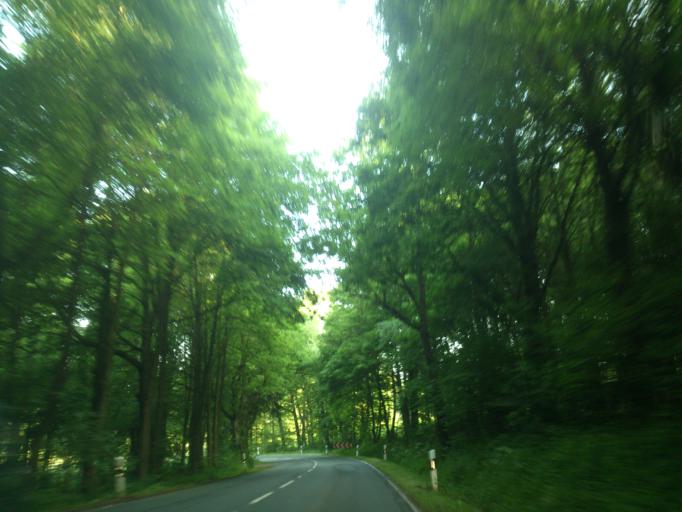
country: DE
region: North Rhine-Westphalia
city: Lichtenau
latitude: 51.6621
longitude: 8.9463
